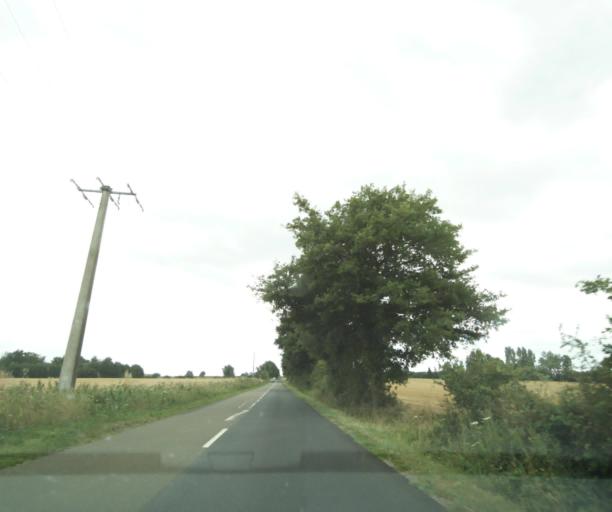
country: FR
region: Pays de la Loire
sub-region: Departement de Maine-et-Loire
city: Durtal
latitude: 47.7318
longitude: -0.2646
